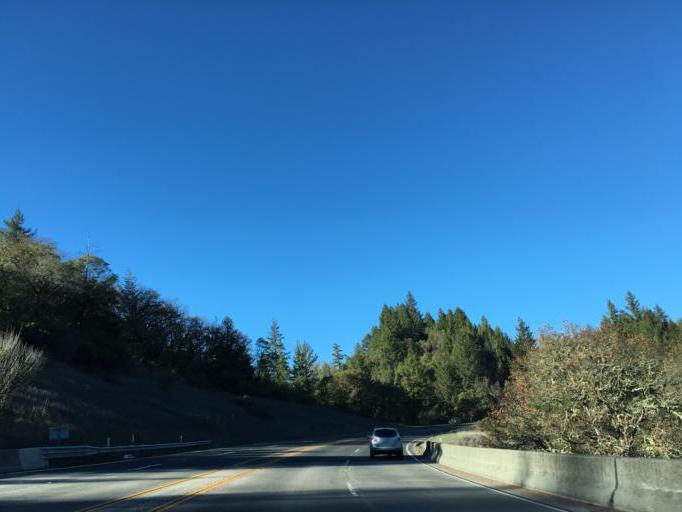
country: US
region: California
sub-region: Mendocino County
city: Brooktrails
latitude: 39.5367
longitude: -123.4167
